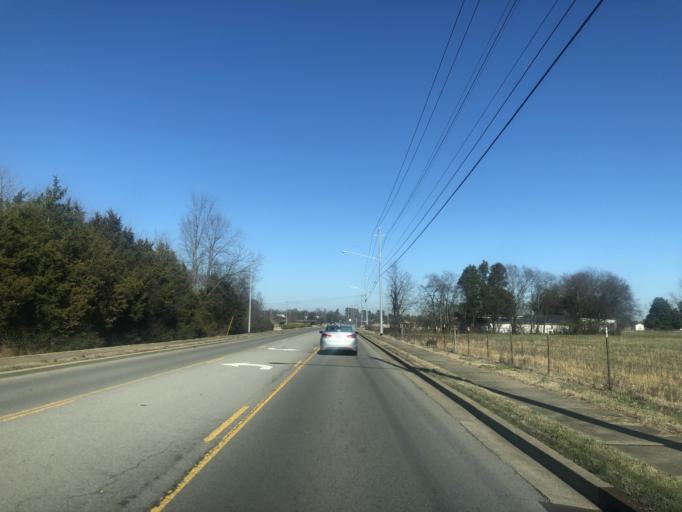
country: US
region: Tennessee
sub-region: Rutherford County
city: Smyrna
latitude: 35.9169
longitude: -86.4686
